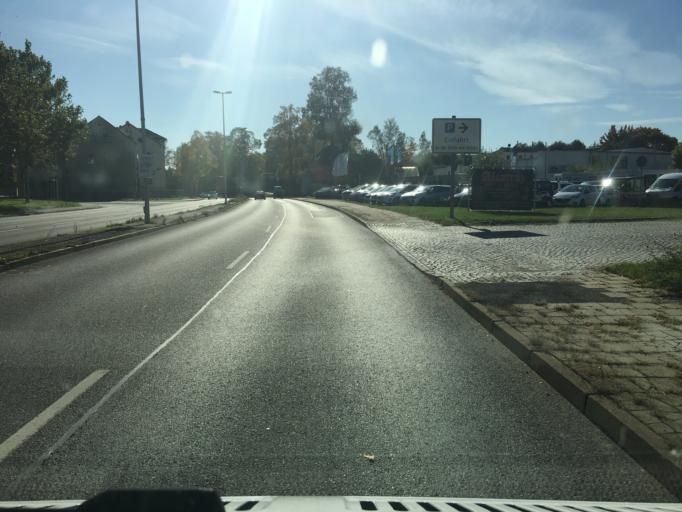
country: DE
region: Saxony
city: Zwickau
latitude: 50.7141
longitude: 12.4999
